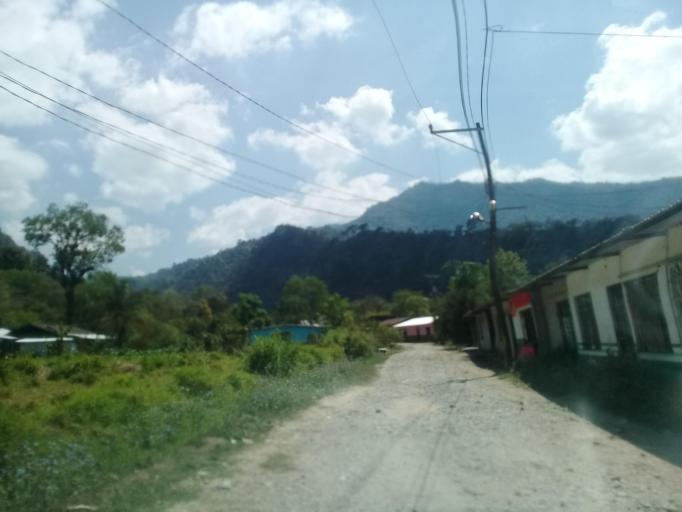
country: MX
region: Veracruz
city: Jalapilla
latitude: 18.8130
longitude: -97.0649
